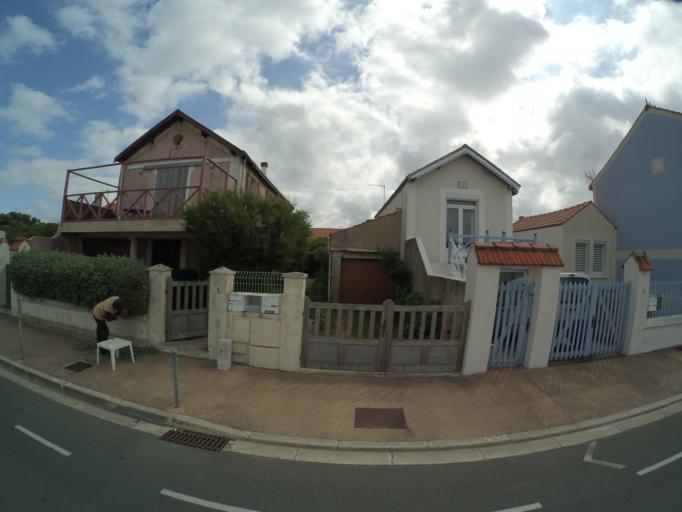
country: FR
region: Poitou-Charentes
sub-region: Departement de la Charente-Maritime
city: Chatelaillon-Plage
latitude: 46.0825
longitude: -1.0960
